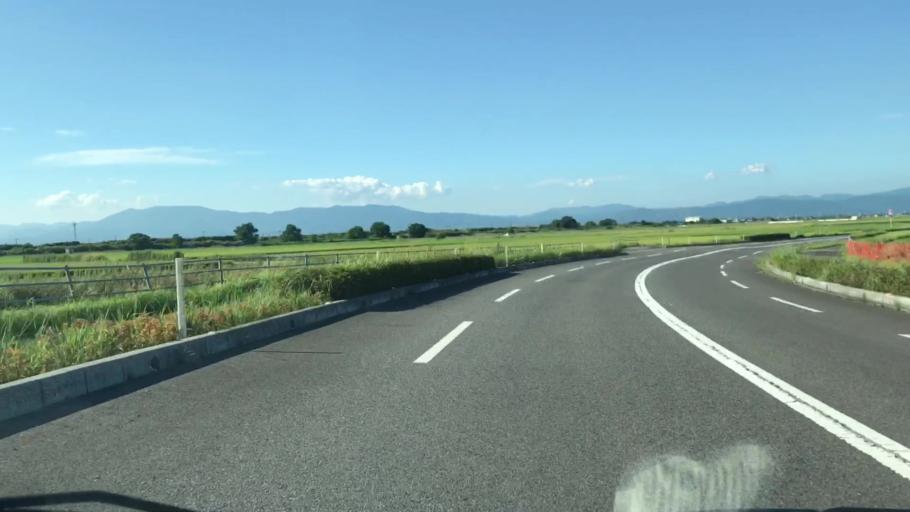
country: JP
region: Saga Prefecture
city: Okawa
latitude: 33.1608
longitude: 130.2900
